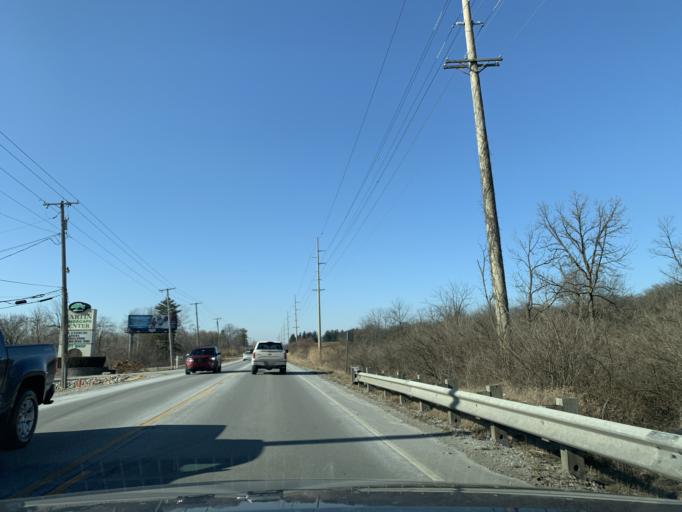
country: US
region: Indiana
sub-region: Lake County
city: Saint John
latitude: 41.4211
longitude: -87.4550
